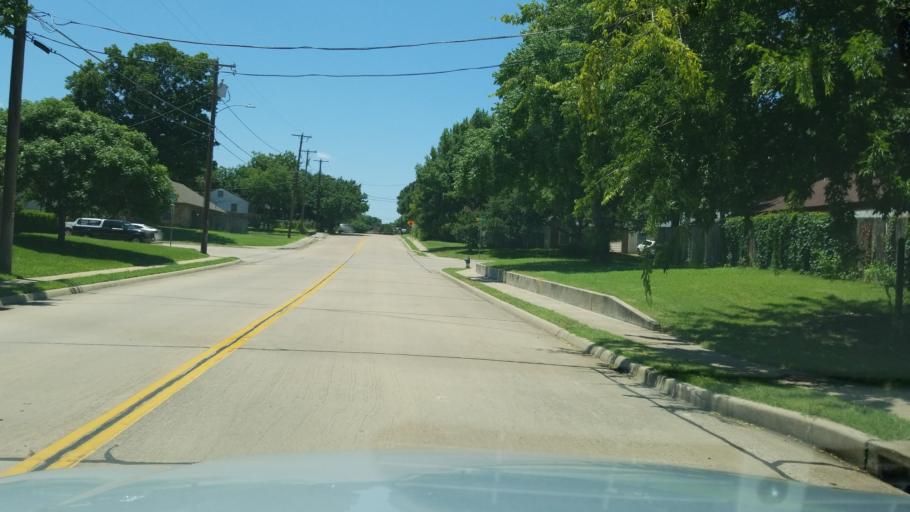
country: US
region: Texas
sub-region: Dallas County
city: Irving
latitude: 32.7975
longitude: -96.9278
